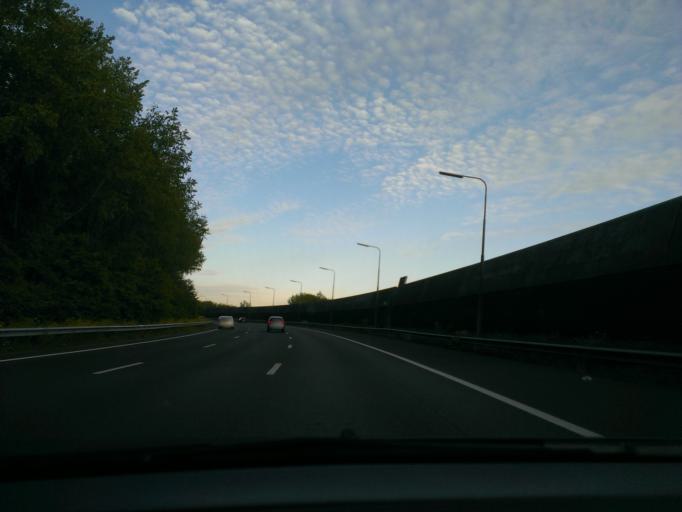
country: NL
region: South Holland
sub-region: Gemeente Ridderkerk
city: Ridderkerk
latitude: 51.8570
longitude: 4.5942
